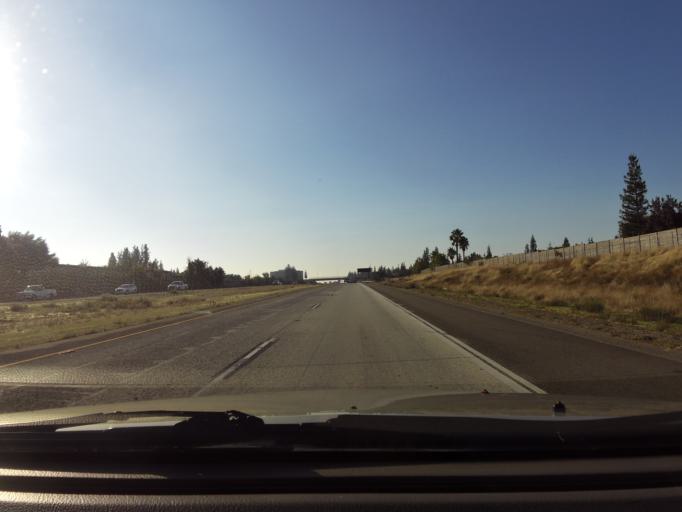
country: US
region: California
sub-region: Fresno County
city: Clovis
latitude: 36.8667
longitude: -119.7920
